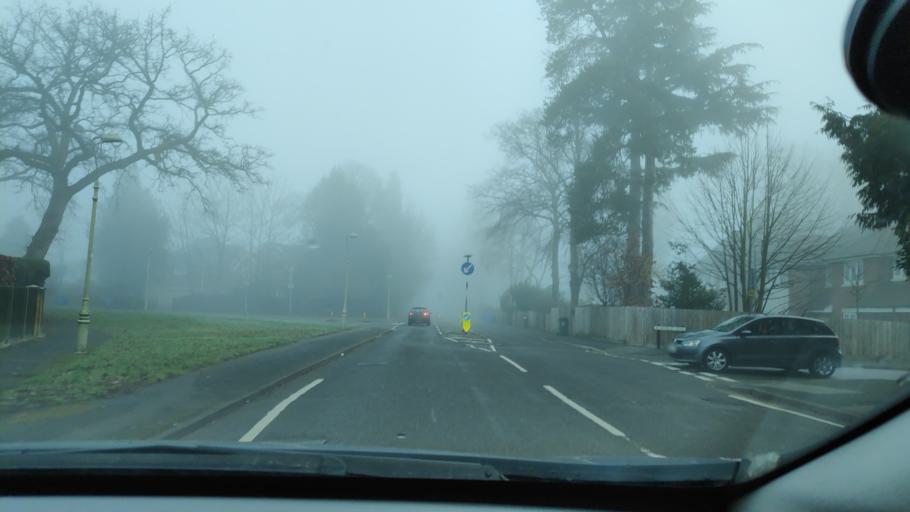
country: GB
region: England
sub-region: Hampshire
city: Farnborough
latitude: 51.2894
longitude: -0.7454
